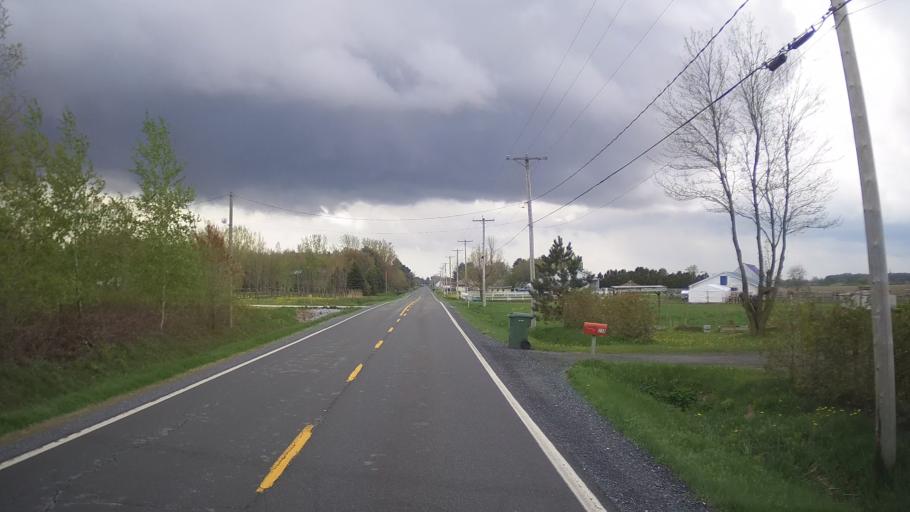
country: CA
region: Quebec
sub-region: Monteregie
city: Marieville
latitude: 45.3200
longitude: -73.1088
